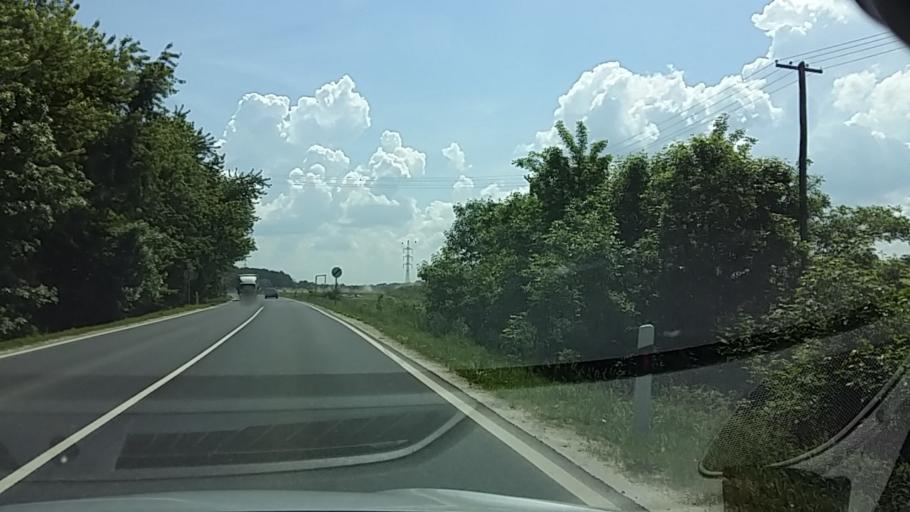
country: AT
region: Burgenland
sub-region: Politischer Bezirk Gussing
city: Heiligenbrunn
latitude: 46.9740
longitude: 16.3803
